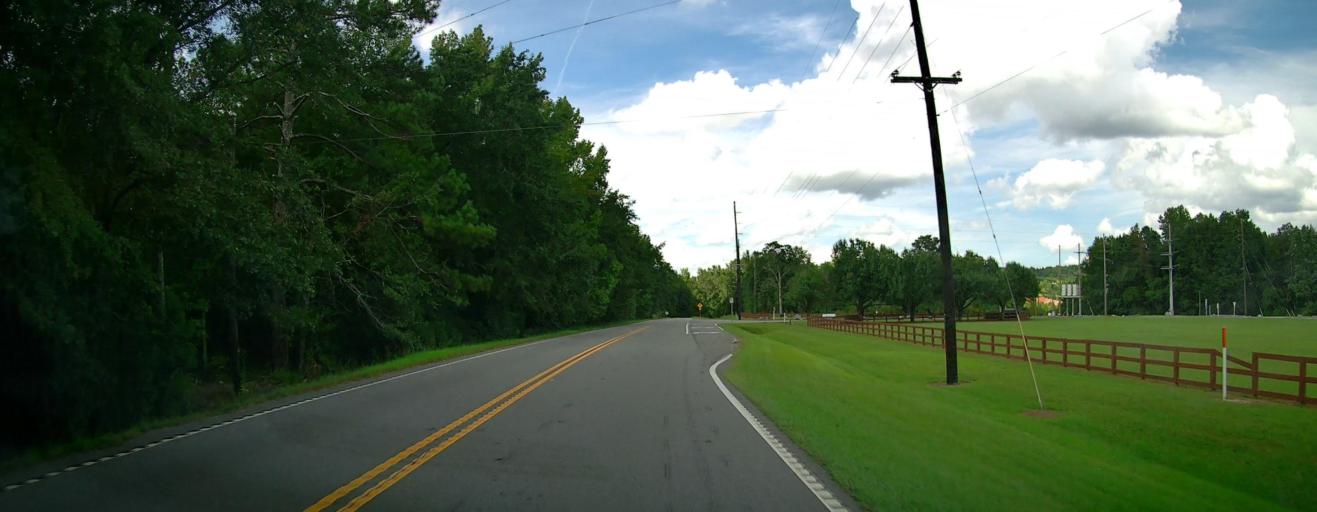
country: US
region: Georgia
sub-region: Talbot County
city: Talbotton
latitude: 32.6182
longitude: -84.4880
